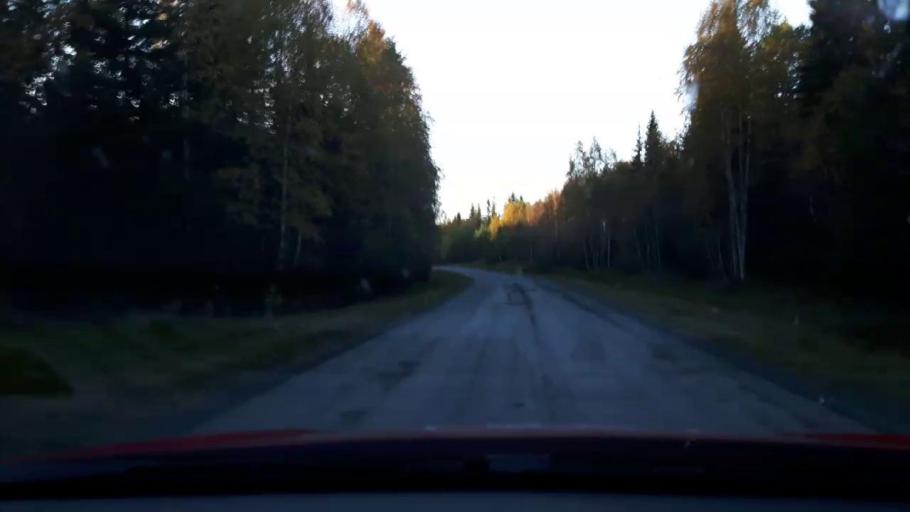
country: SE
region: Jaemtland
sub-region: Krokoms Kommun
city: Krokom
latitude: 63.4597
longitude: 14.3980
